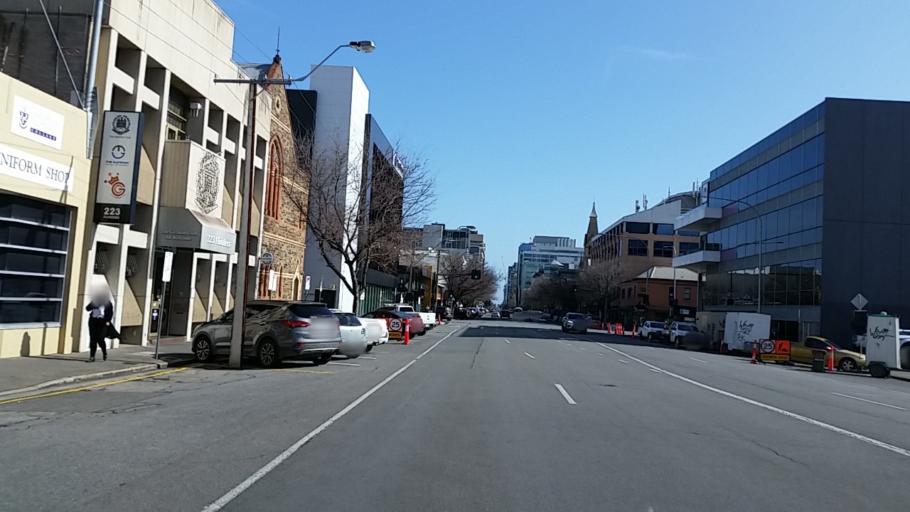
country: AU
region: South Australia
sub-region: Adelaide
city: Adelaide
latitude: -34.9267
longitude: 138.6093
